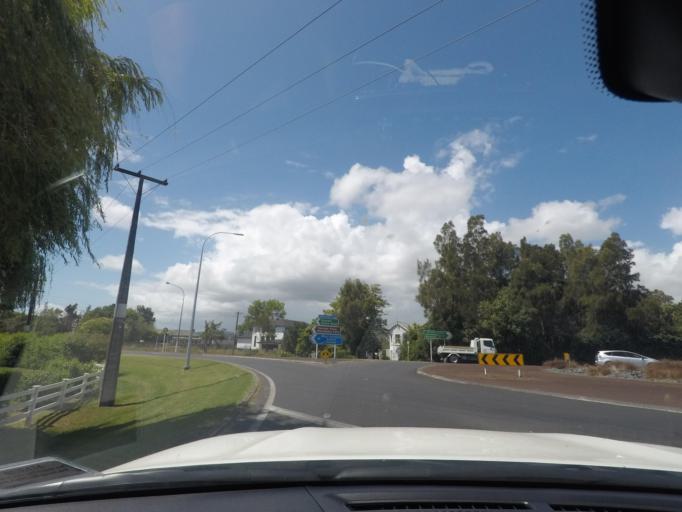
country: NZ
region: Auckland
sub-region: Auckland
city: Parakai
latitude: -36.6734
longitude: 174.4412
